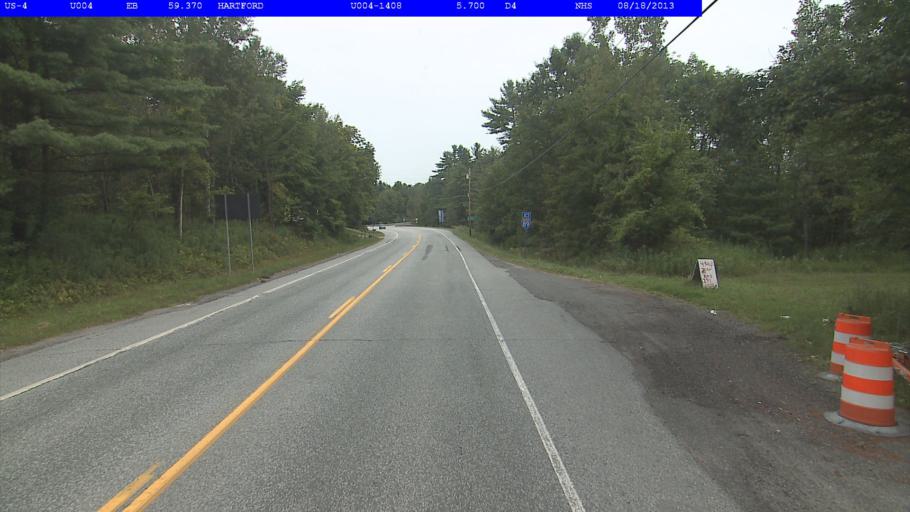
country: US
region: Vermont
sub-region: Windsor County
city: White River Junction
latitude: 43.6598
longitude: -72.3874
